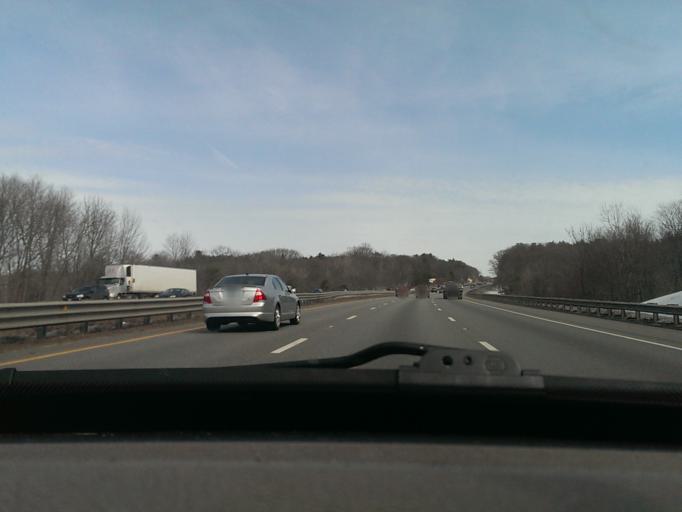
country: US
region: Massachusetts
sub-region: Worcester County
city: Charlton
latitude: 42.1467
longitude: -72.0115
